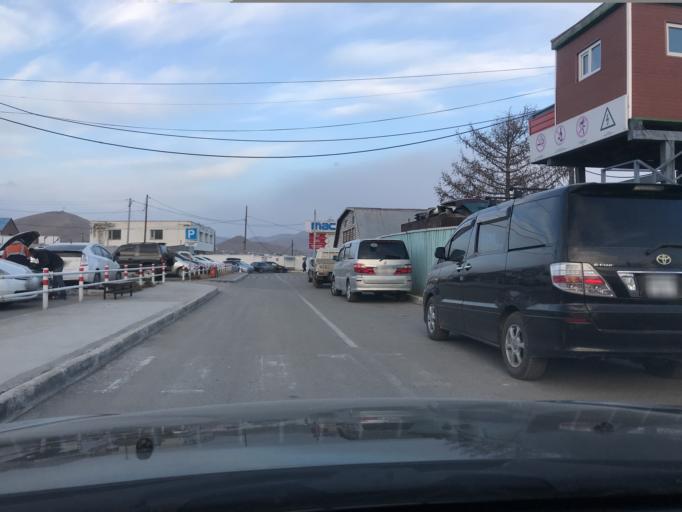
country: MN
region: Ulaanbaatar
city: Ulaanbaatar
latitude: 47.9305
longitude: 106.9999
